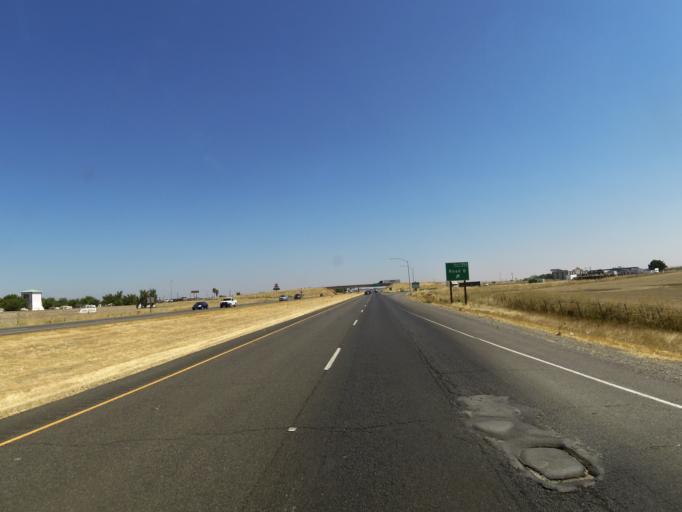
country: US
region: California
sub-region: Yolo County
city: Dunnigan
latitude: 38.8644
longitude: -121.9573
